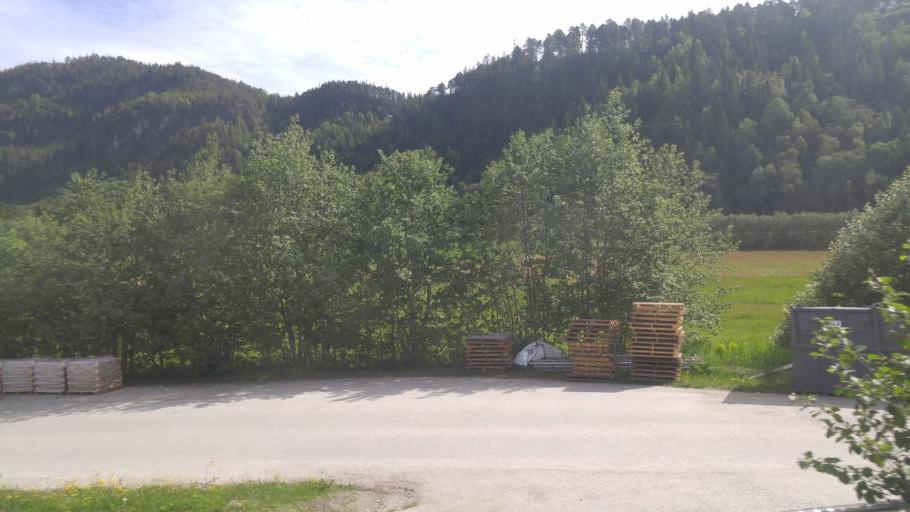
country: NO
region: Sor-Trondelag
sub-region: Midtre Gauldal
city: Storen
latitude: 63.0408
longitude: 10.2940
